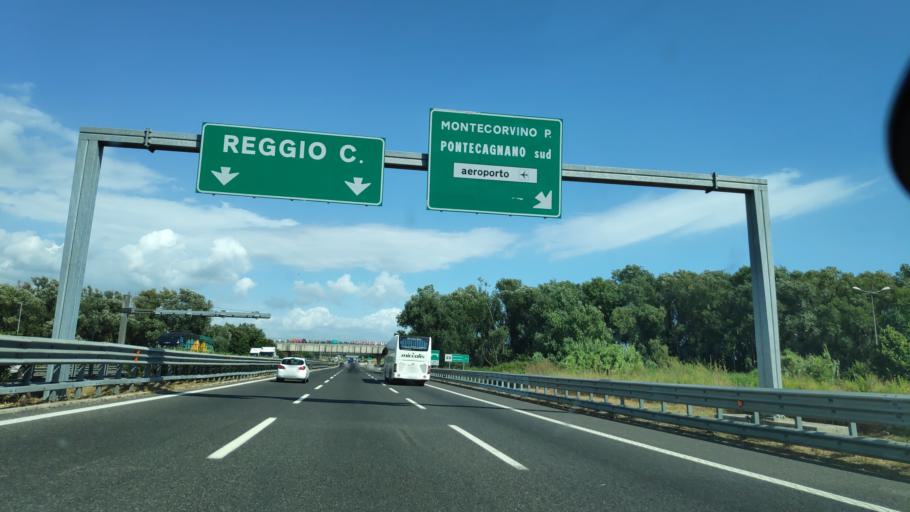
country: IT
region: Campania
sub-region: Provincia di Salerno
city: Pagliarone
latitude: 40.6359
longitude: 14.9117
